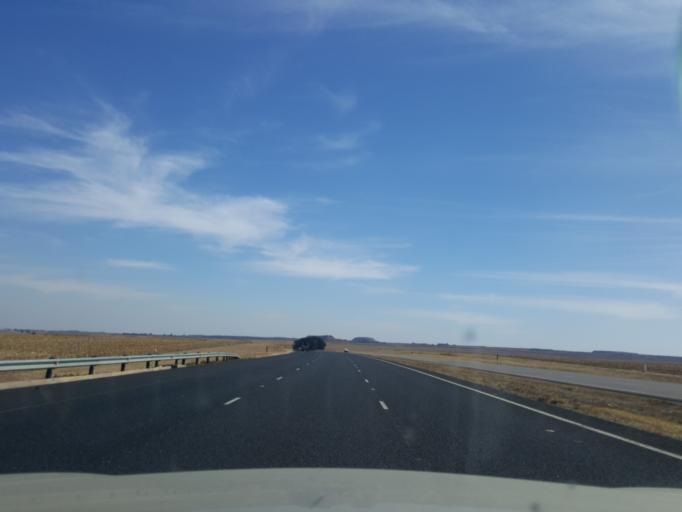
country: ZA
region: Mpumalanga
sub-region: Nkangala District Municipality
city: Belfast
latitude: -25.8289
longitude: 29.7666
